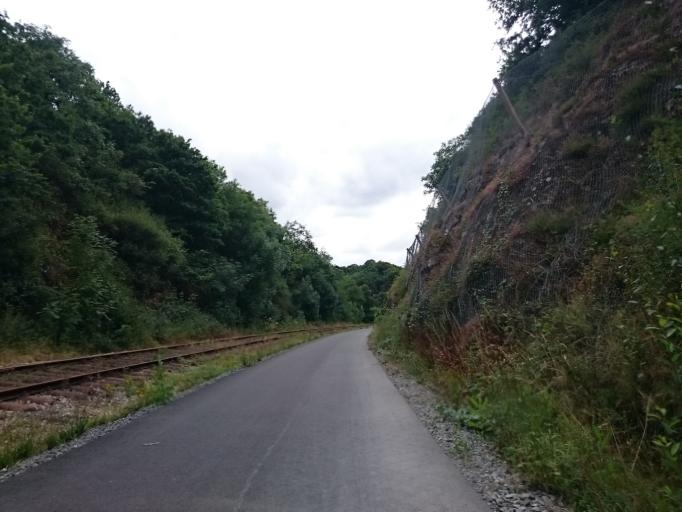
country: FR
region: Lower Normandy
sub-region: Departement du Calvados
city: Clinchamps-sur-Orne
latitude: 49.0645
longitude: -0.4441
